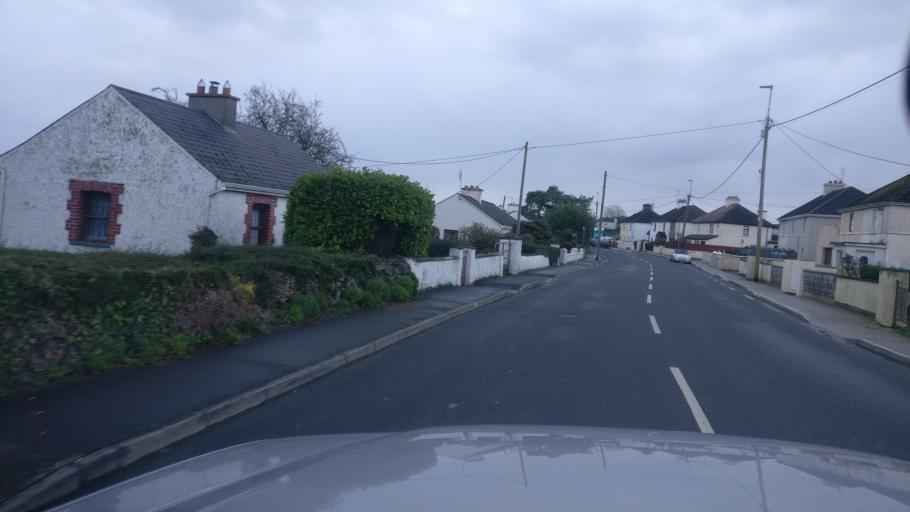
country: IE
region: Munster
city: Nenagh Bridge
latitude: 52.9940
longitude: -8.1263
